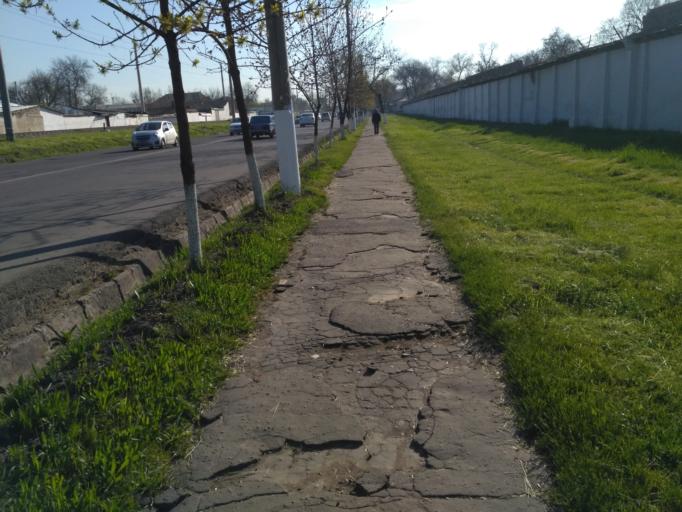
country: UZ
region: Toshkent Shahri
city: Tashkent
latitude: 41.2688
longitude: 69.2714
